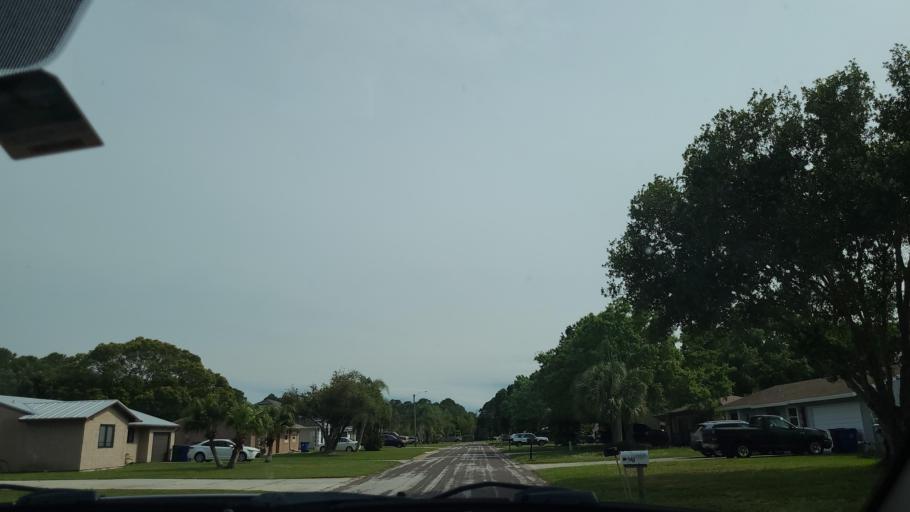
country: US
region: Florida
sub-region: Indian River County
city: Sebastian
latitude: 27.7726
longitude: -80.4694
